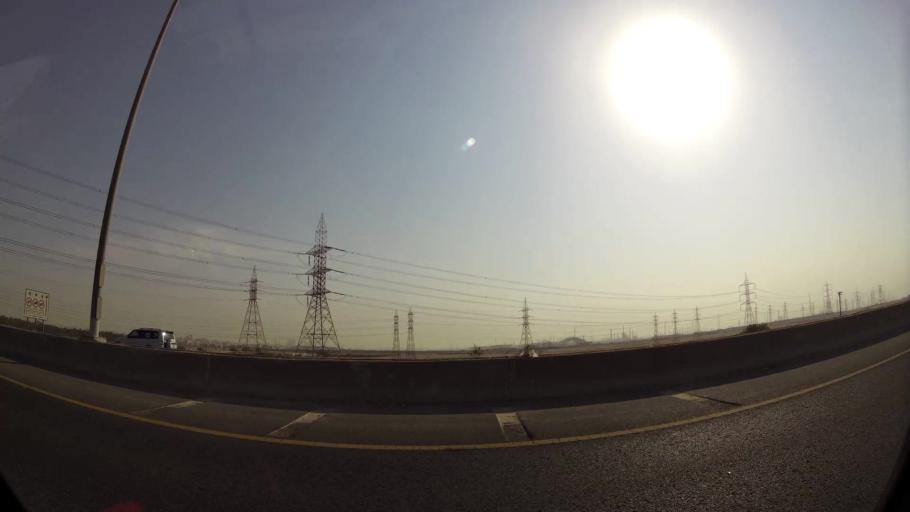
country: KW
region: Al Ahmadi
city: Al Ahmadi
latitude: 29.0705
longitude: 48.0991
